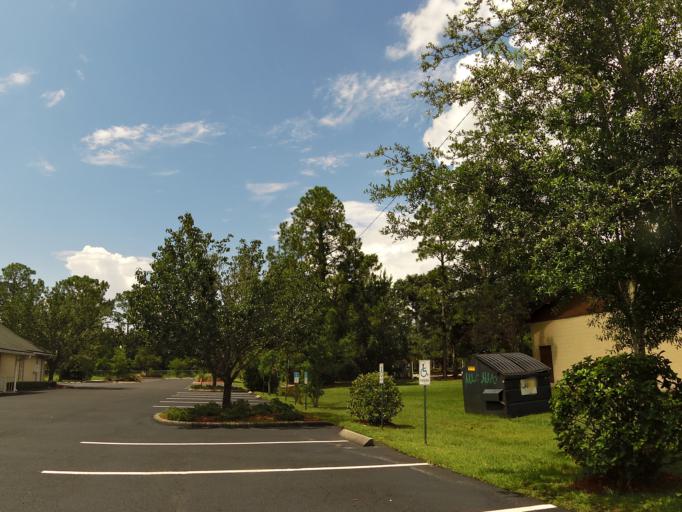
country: US
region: Florida
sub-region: Saint Johns County
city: Fruit Cove
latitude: 30.1498
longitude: -81.6336
